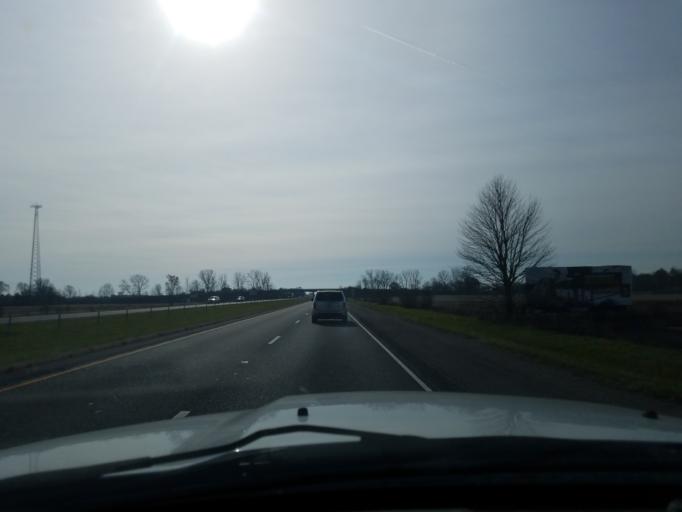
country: US
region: Indiana
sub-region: Delaware County
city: Daleville
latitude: 40.1825
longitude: -85.5627
